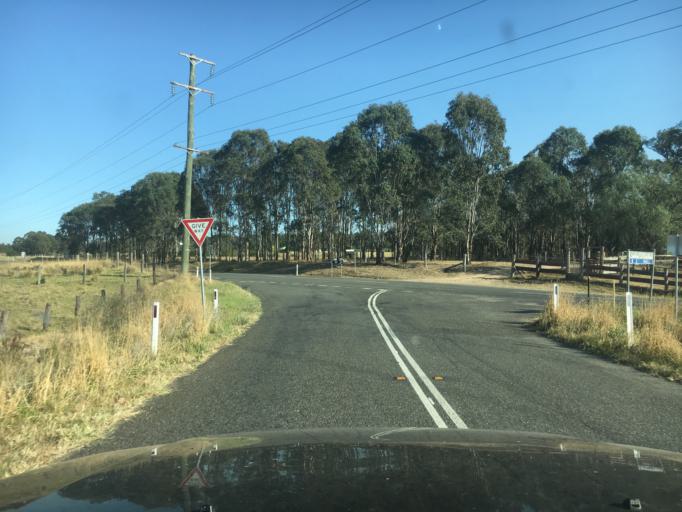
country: AU
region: New South Wales
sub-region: Singleton
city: Singleton
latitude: -32.5469
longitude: 151.2645
